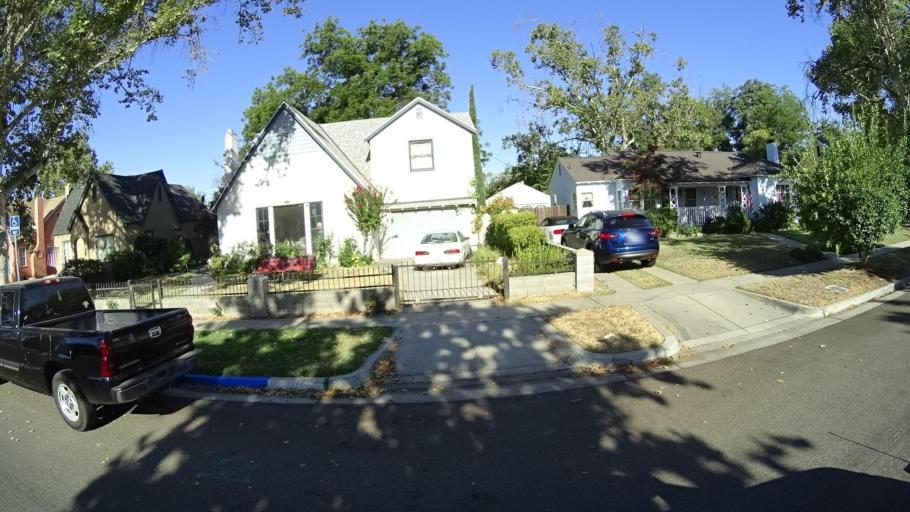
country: US
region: California
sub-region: Fresno County
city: Fresno
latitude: 36.7618
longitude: -119.7923
